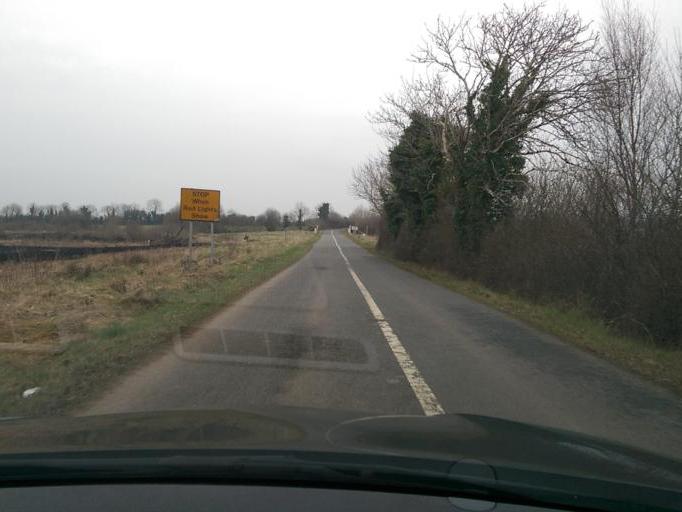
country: IE
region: Leinster
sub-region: An Longfort
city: Longford
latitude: 53.6528
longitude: -7.8655
